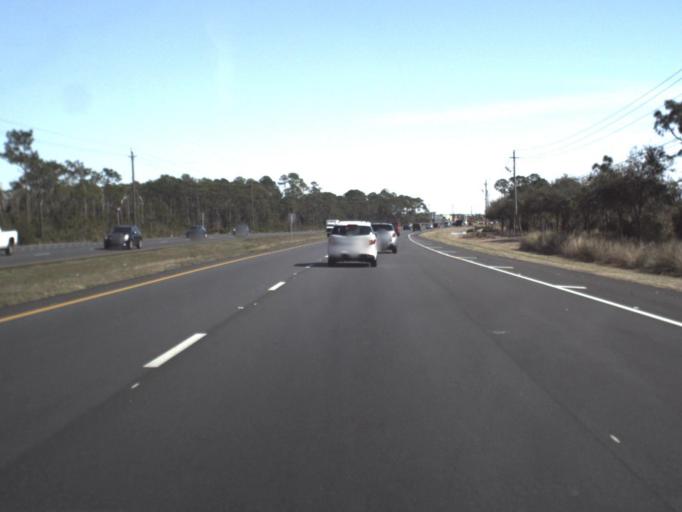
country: US
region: Florida
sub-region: Bay County
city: Laguna Beach
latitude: 30.2265
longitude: -85.8768
